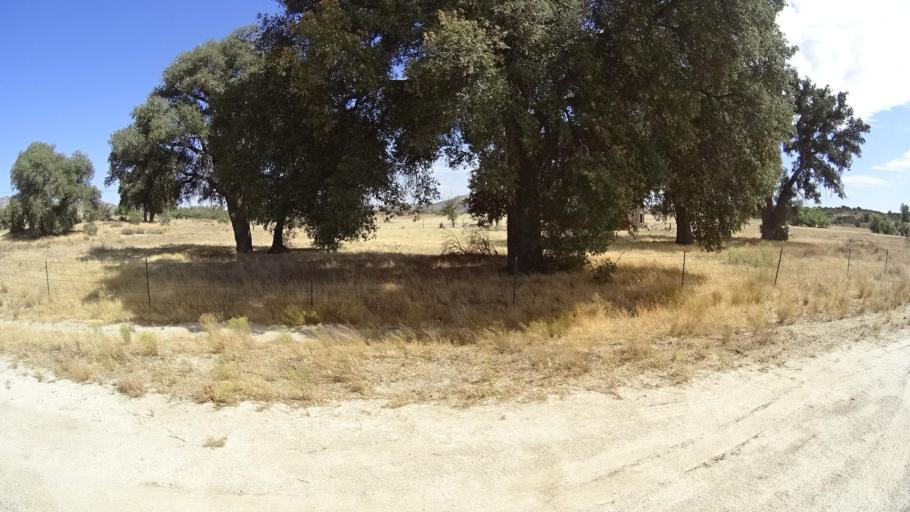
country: MX
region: Baja California
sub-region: Tecate
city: Cereso del Hongo
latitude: 32.6863
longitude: -116.2626
